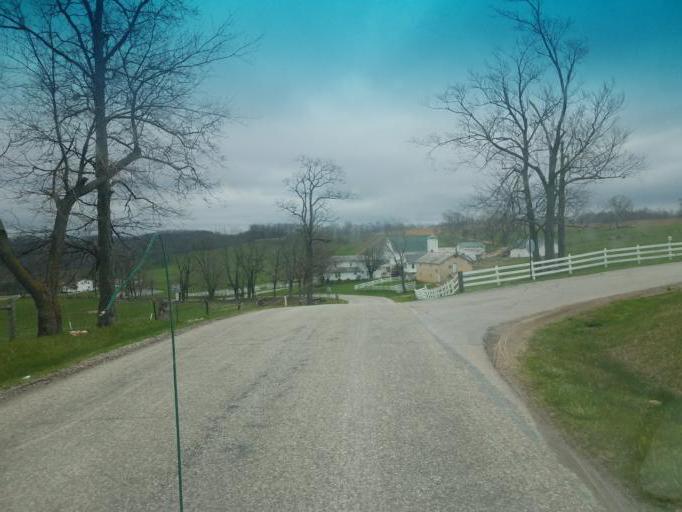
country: US
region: Ohio
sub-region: Stark County
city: Beach City
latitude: 40.6209
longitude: -81.6731
